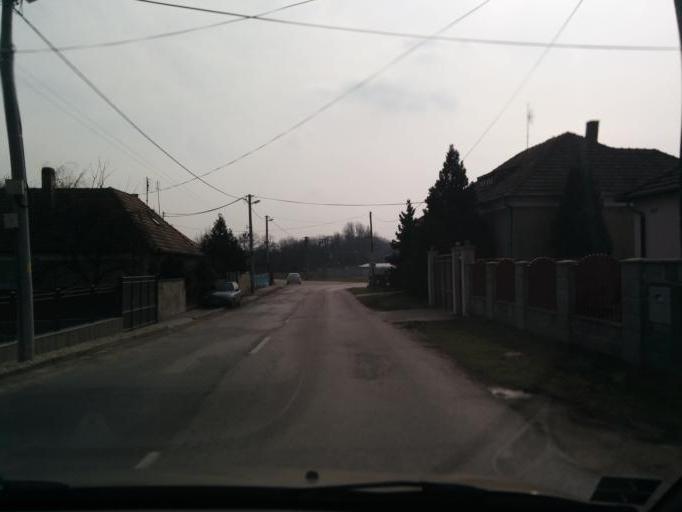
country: SK
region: Trnavsky
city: Sladkovicovo
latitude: 48.2231
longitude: 17.6359
